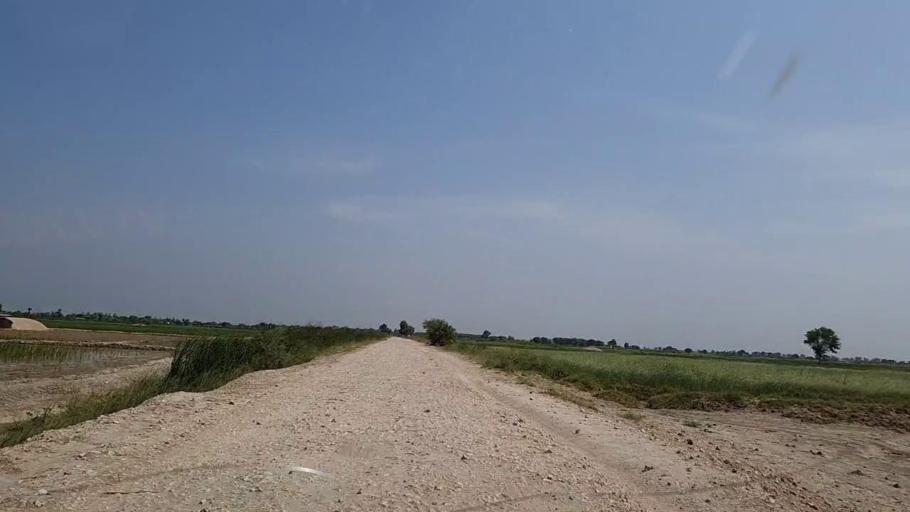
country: PK
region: Sindh
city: Khanpur
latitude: 27.7963
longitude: 69.3149
